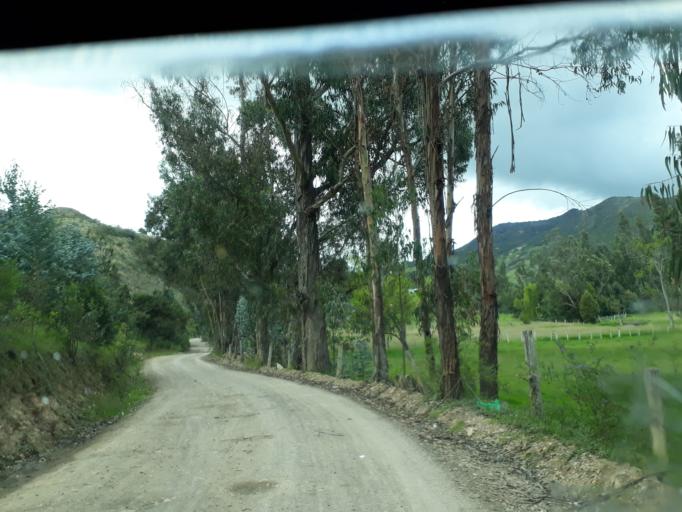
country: CO
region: Cundinamarca
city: Cucunuba
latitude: 5.2635
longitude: -73.7714
